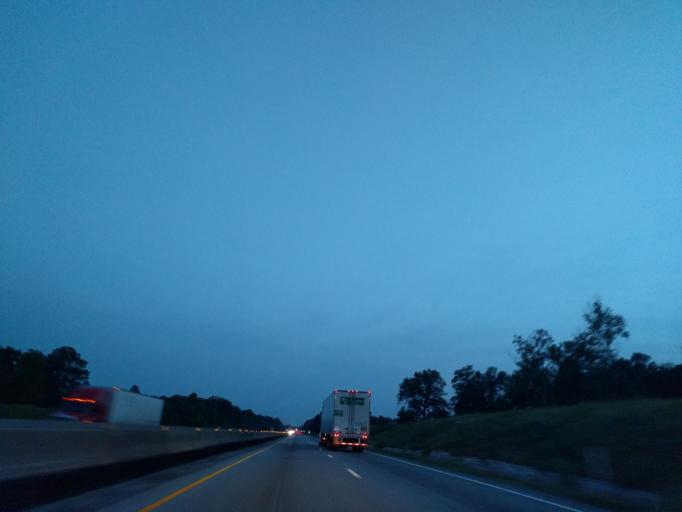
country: US
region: Kentucky
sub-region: Hardin County
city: Elizabethtown
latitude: 37.6531
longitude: -85.8565
